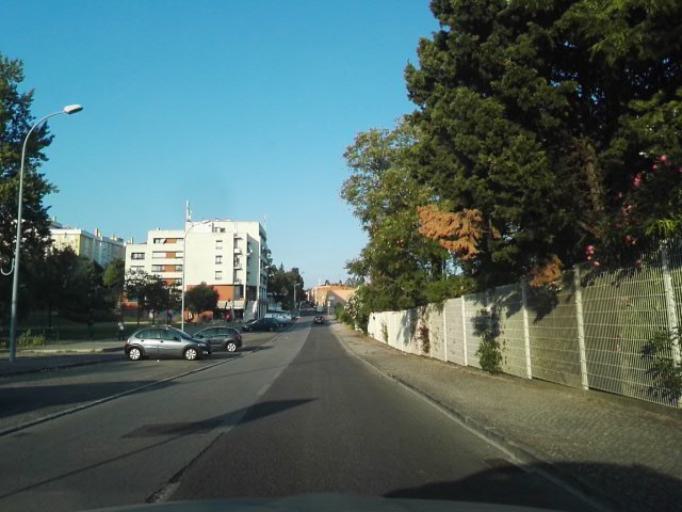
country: PT
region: Lisbon
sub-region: Amadora
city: Amadora
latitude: 38.7334
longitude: -9.2120
